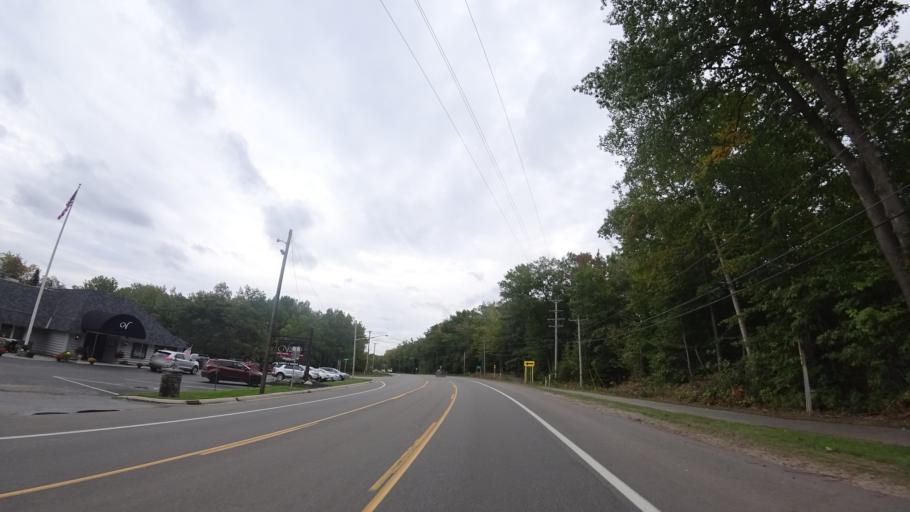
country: US
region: Michigan
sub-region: Emmet County
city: Petoskey
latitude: 45.4140
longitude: -84.9045
